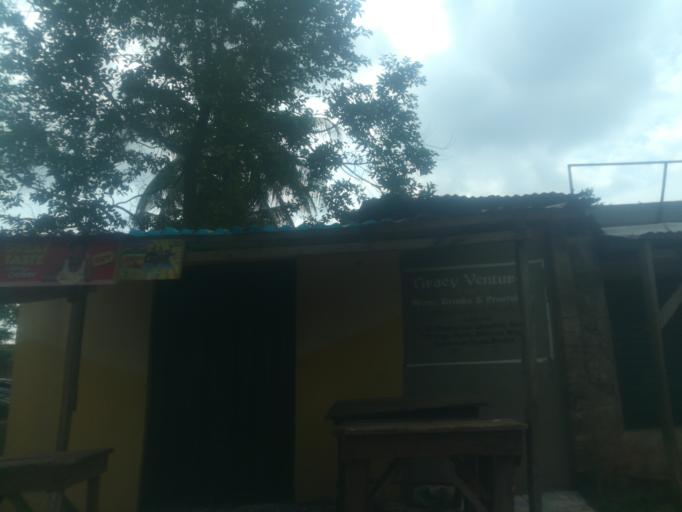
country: NG
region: Oyo
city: Ibadan
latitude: 7.4196
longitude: 3.9314
